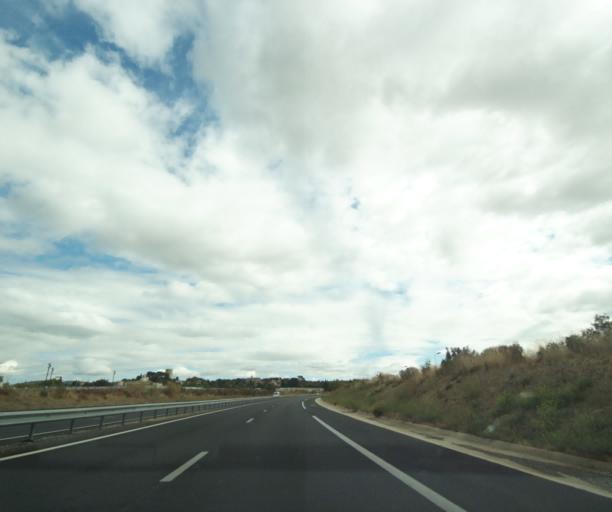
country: FR
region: Languedoc-Roussillon
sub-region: Departement de l'Herault
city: Gignac
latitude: 43.6511
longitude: 3.5398
